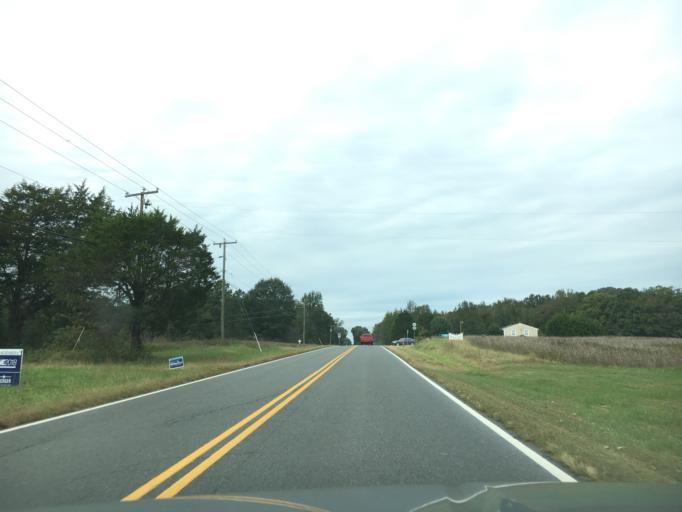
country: US
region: Virginia
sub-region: Goochland County
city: Goochland
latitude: 37.7519
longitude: -77.8616
